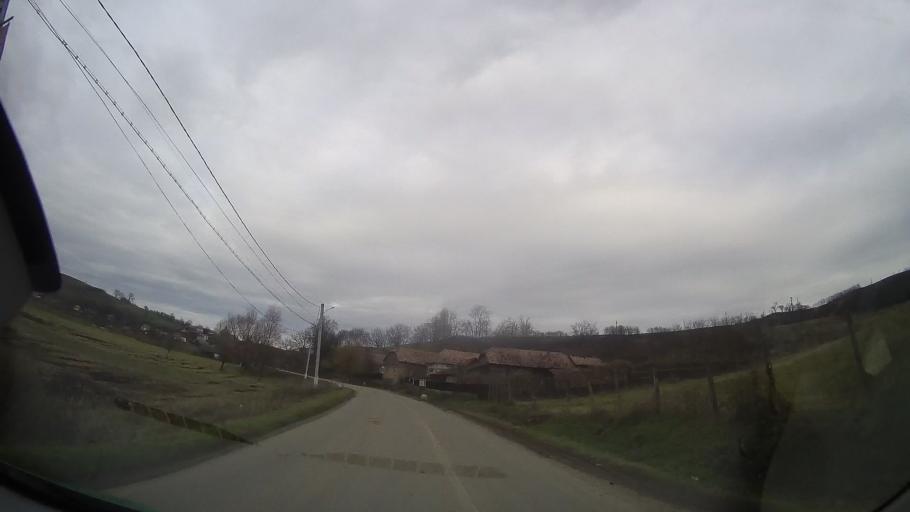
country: RO
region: Mures
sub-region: Comuna Faragau
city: Faragau
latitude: 46.7566
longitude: 24.5182
